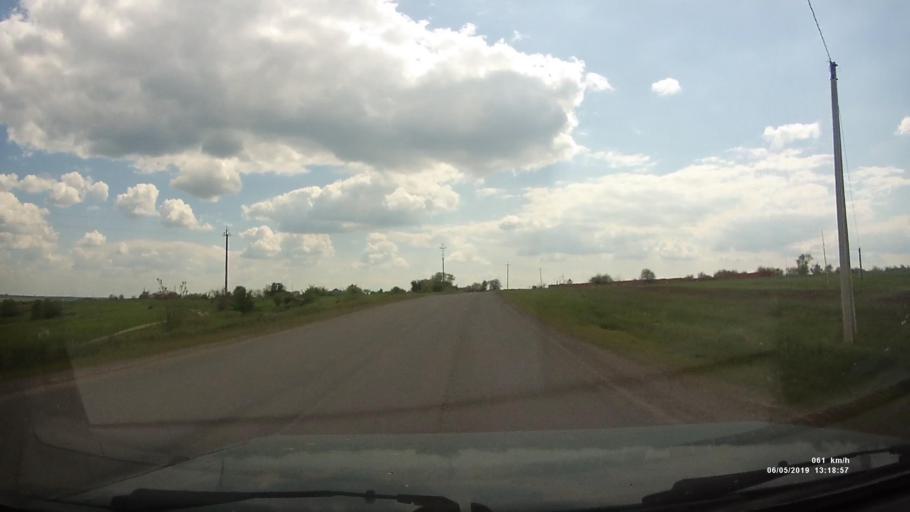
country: RU
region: Rostov
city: Ust'-Donetskiy
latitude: 47.7297
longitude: 40.9141
